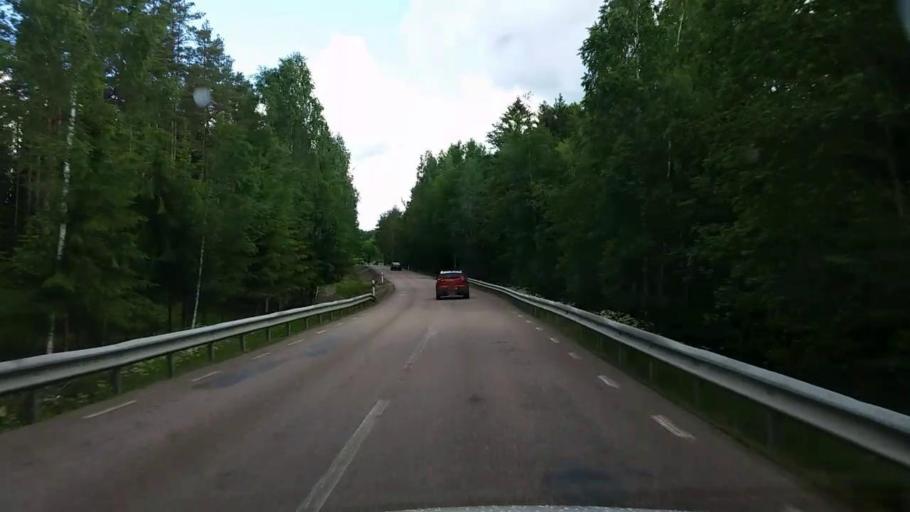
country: SE
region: Vaestmanland
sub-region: Skinnskattebergs Kommun
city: Skinnskatteberg
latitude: 59.8458
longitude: 15.8412
